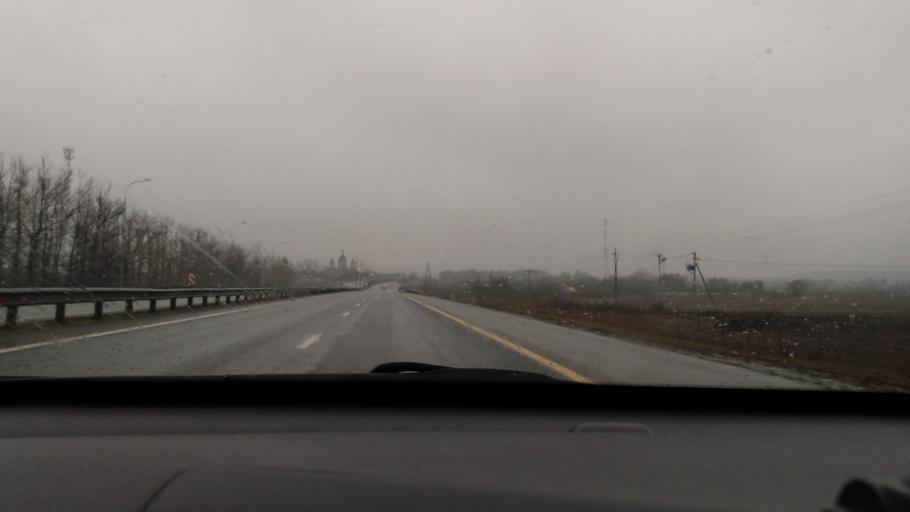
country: RU
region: Tula
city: Gritsovskiy
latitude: 54.2485
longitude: 38.1442
